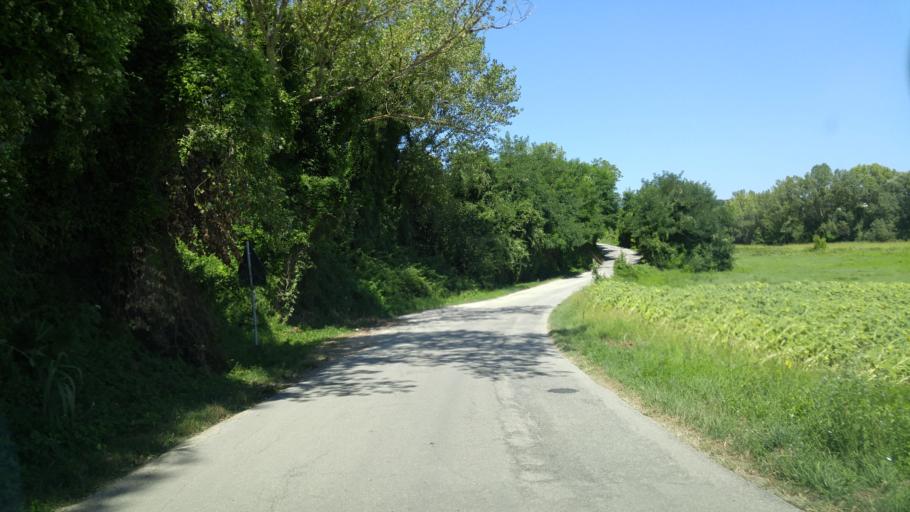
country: IT
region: The Marches
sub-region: Provincia di Pesaro e Urbino
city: Fenile
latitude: 43.8343
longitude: 12.9711
